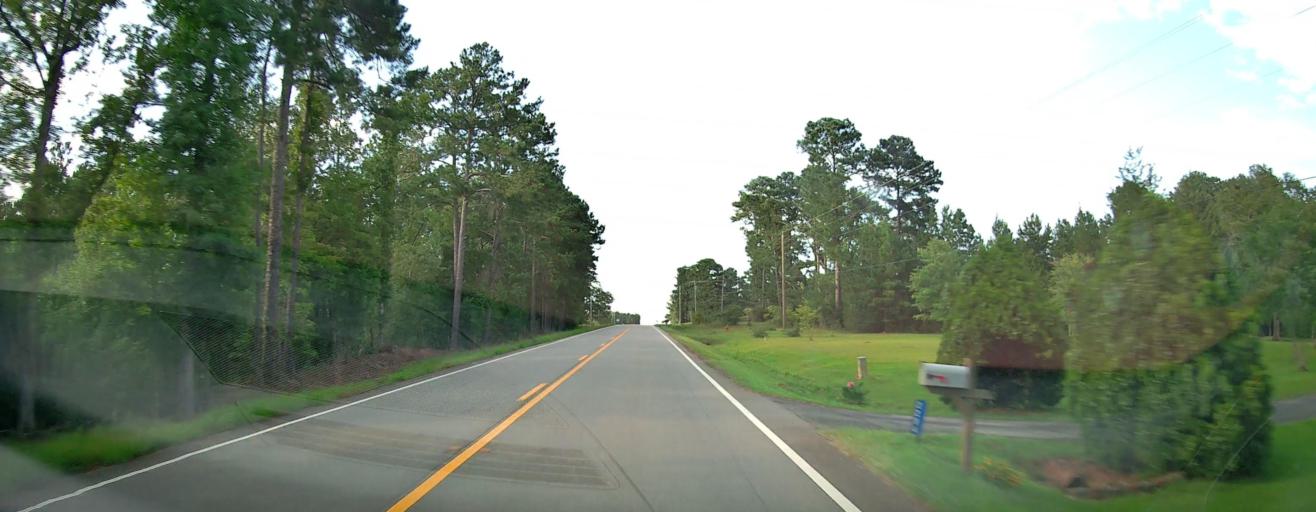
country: US
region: Georgia
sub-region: Monroe County
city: Forsyth
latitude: 32.9759
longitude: -83.9538
